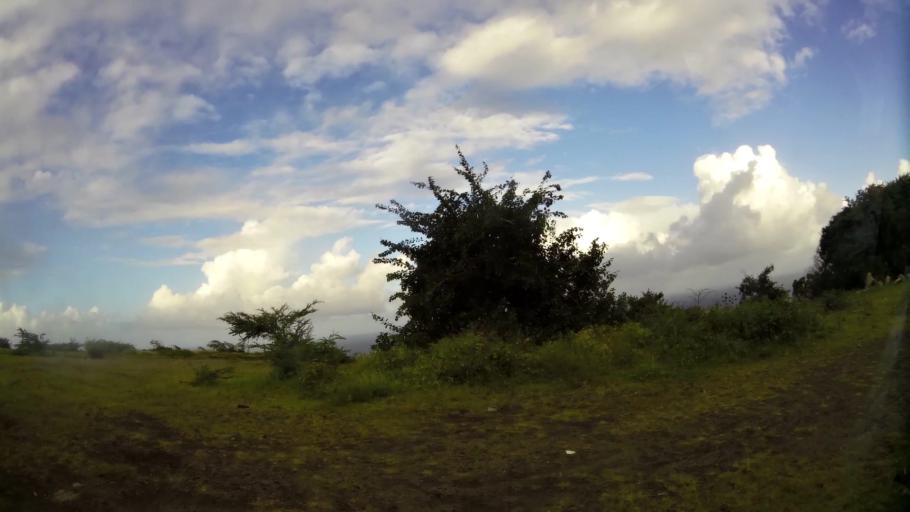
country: MS
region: Saint Peter
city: Brades
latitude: 16.7680
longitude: -62.1693
